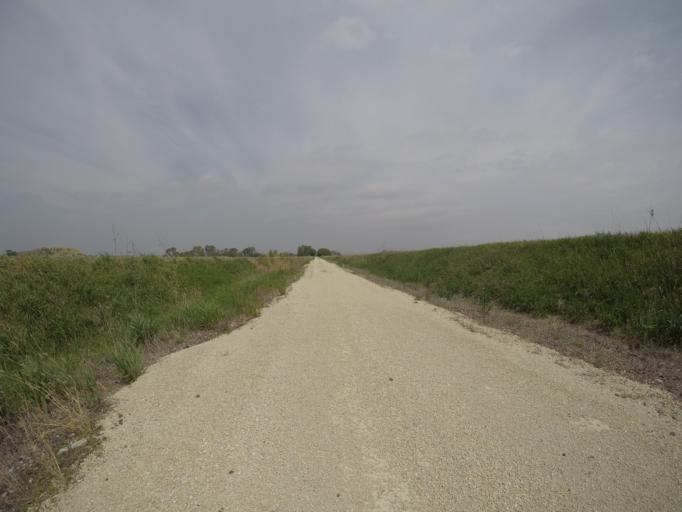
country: US
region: Nebraska
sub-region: Gage County
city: Wymore
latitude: 40.2129
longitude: -96.6623
